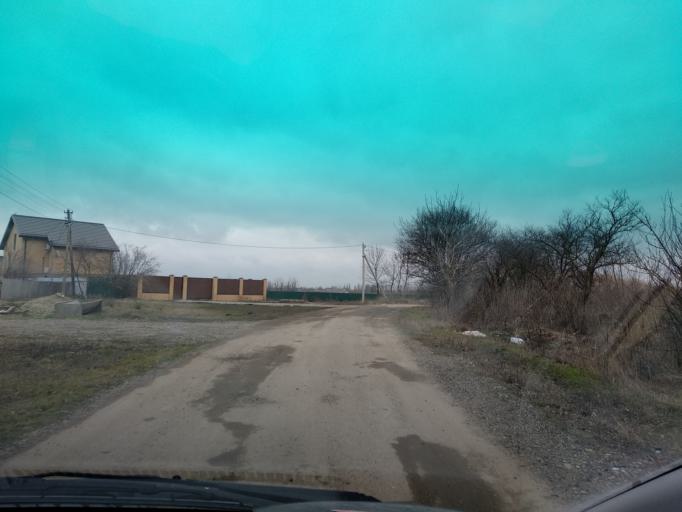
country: RU
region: Krasnodarskiy
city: Vyselki
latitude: 45.6641
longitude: 39.7009
